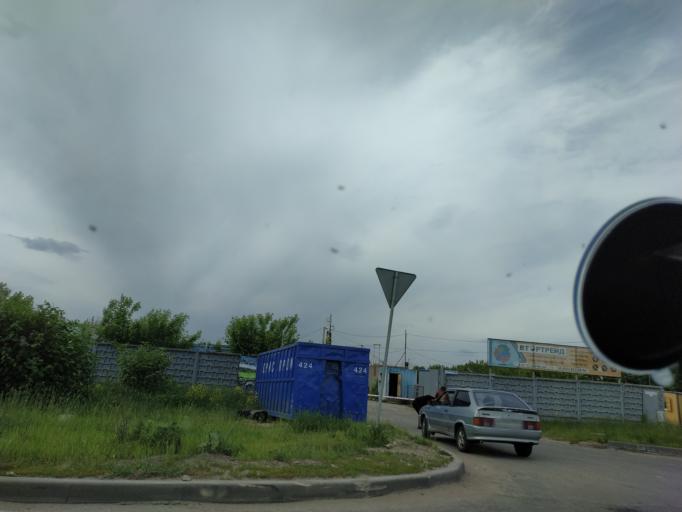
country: RU
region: Moskovskaya
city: Zhukovskiy
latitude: 55.5712
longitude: 38.1153
